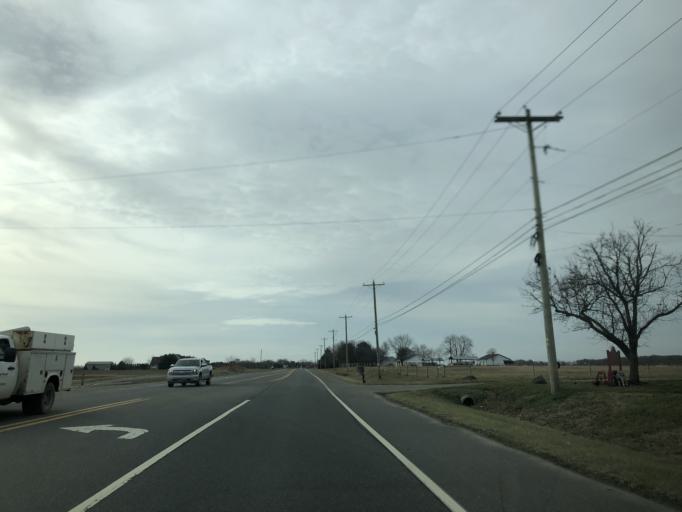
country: US
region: Delaware
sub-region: New Castle County
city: Middletown
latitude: 39.5120
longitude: -75.6793
